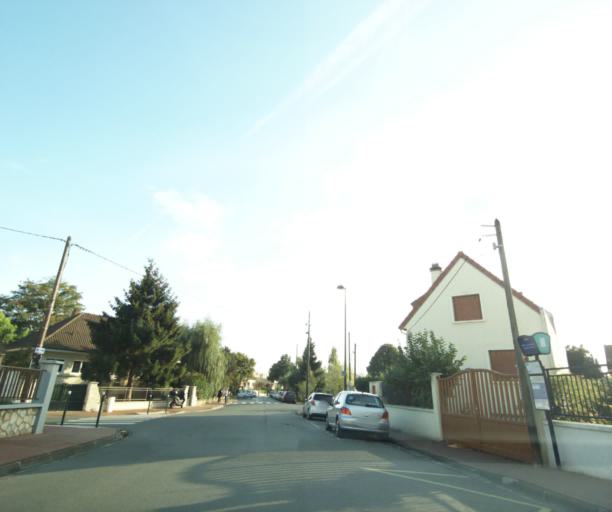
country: FR
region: Ile-de-France
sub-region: Departement de l'Essonne
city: Bievres
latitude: 48.7806
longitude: 2.2331
